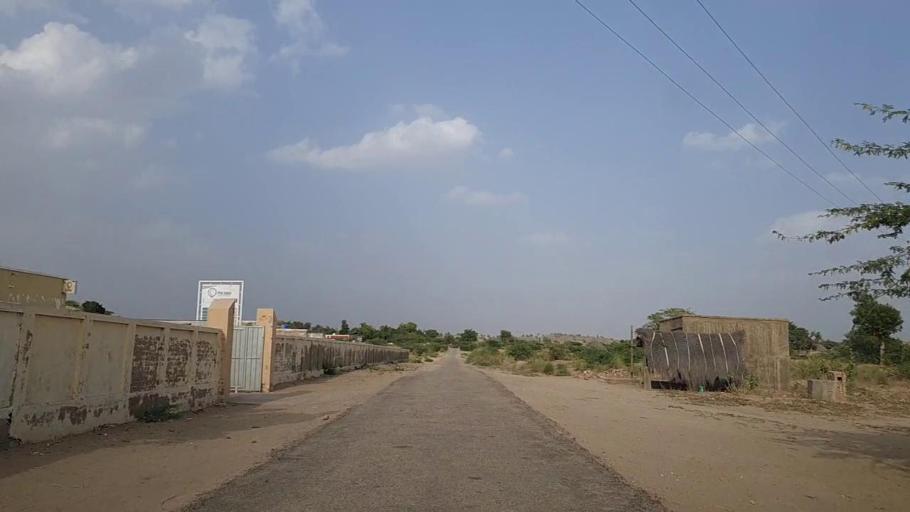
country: PK
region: Sindh
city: Islamkot
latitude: 24.7767
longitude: 70.1900
